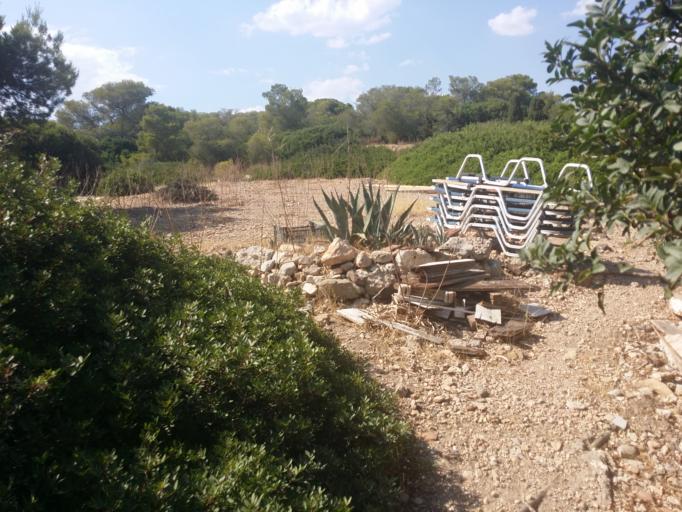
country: GR
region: Attica
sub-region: Nomos Piraios
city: Aegina
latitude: 37.6958
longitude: 23.4339
